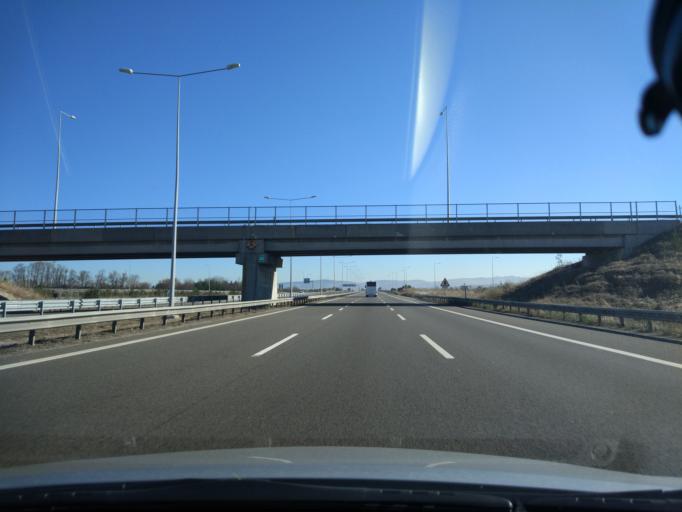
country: TR
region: Bolu
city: Dortdivan
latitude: 40.7431
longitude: 32.1209
